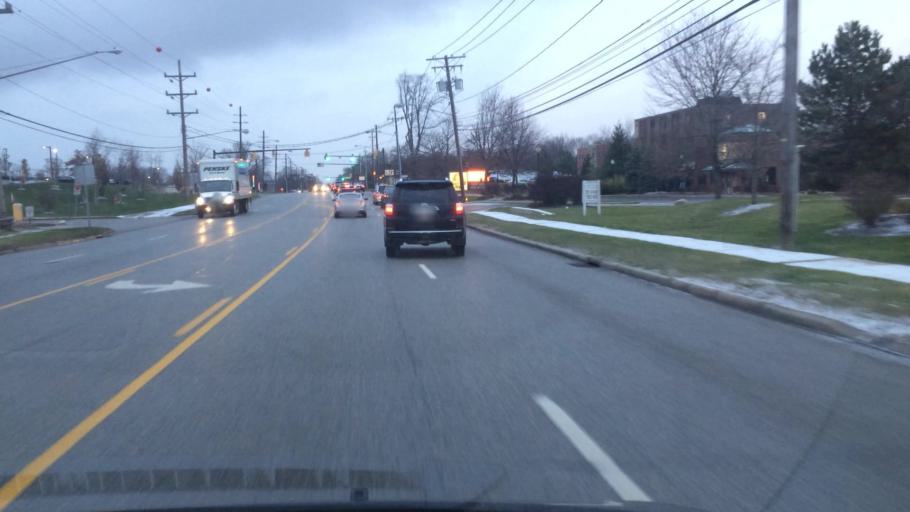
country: US
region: Ohio
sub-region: Cuyahoga County
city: Middleburg Heights
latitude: 41.3721
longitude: -81.8301
